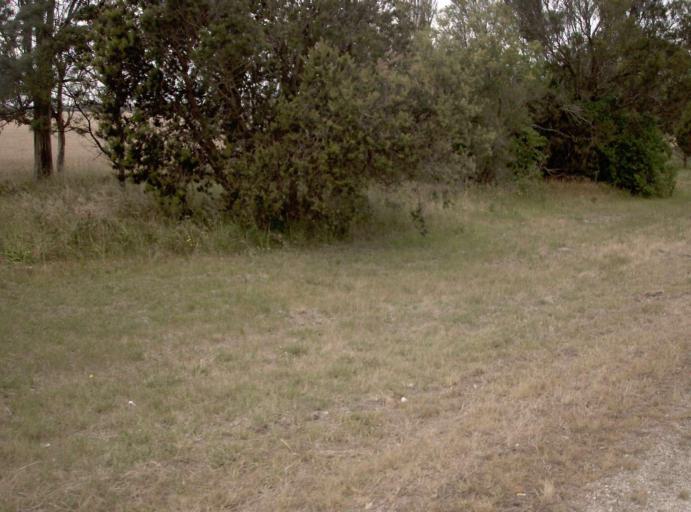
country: AU
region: Victoria
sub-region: Wellington
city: Sale
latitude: -38.1989
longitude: 147.3054
